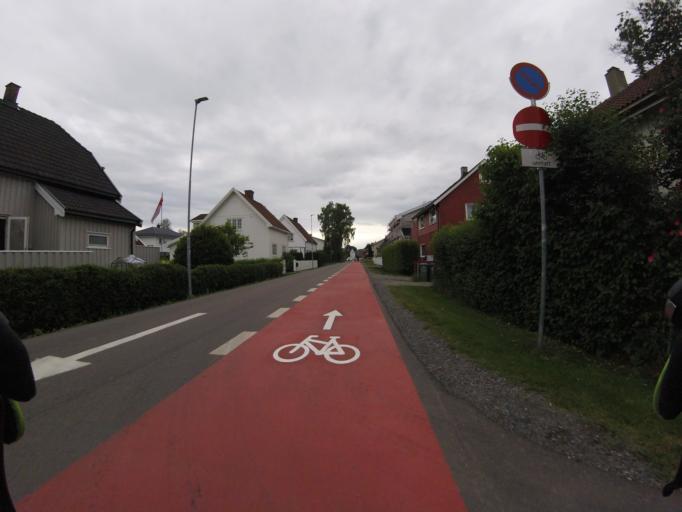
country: NO
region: Akershus
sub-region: Skedsmo
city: Lillestrom
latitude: 59.9618
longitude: 11.0365
